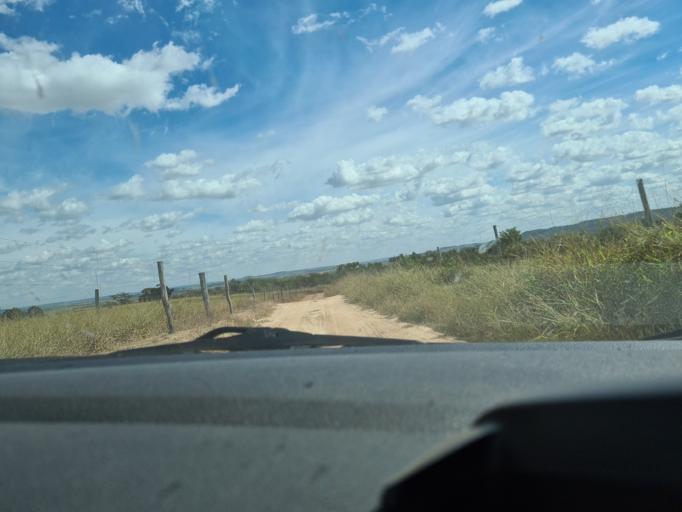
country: BR
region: Goias
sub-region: Silvania
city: Silvania
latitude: -16.5372
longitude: -48.5583
